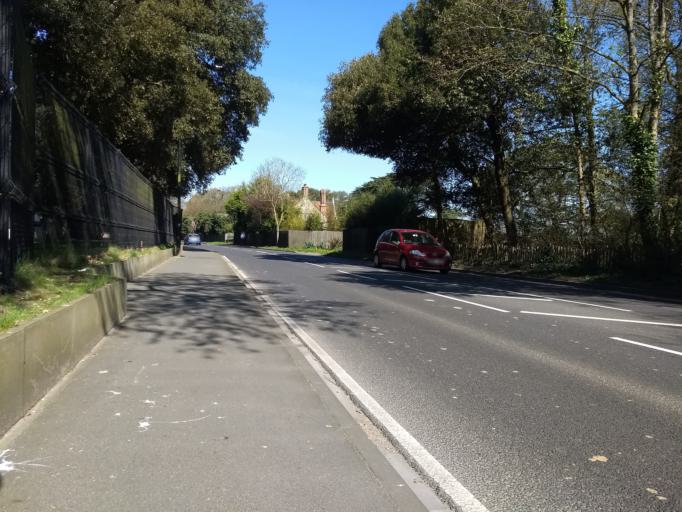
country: GB
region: England
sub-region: Isle of Wight
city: East Cowes
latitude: 50.7434
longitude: -1.2716
